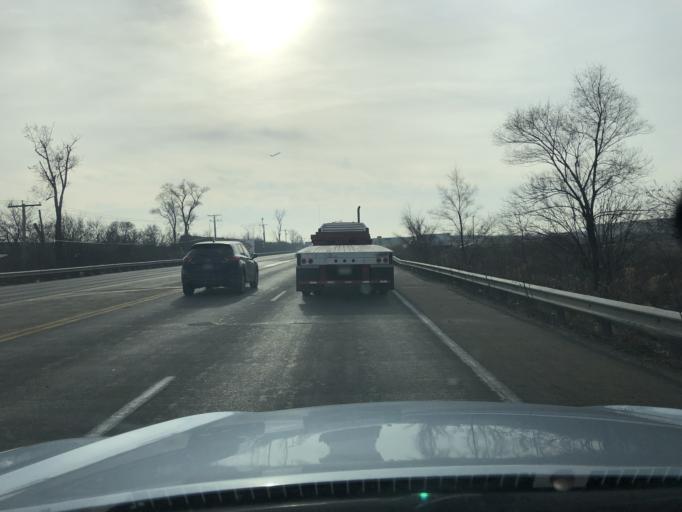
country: US
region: Illinois
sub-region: DuPage County
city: Bensenville
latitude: 41.9857
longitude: -87.9399
